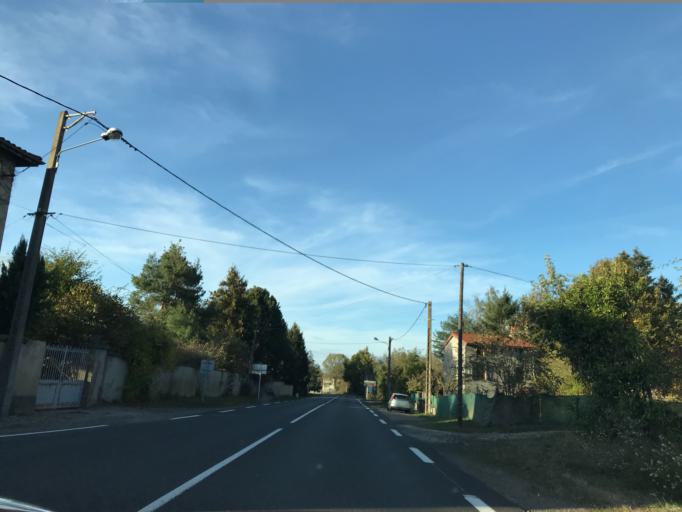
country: FR
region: Auvergne
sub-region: Departement du Puy-de-Dome
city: Paslieres
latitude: 45.9055
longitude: 3.5183
